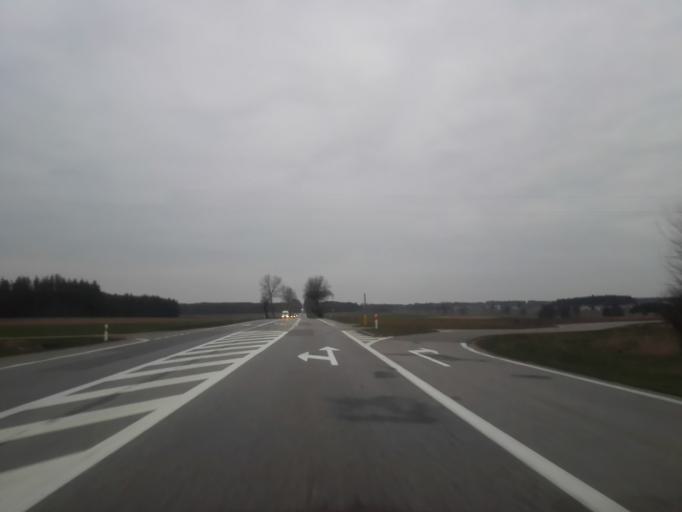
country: PL
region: Podlasie
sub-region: Powiat kolnenski
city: Stawiski
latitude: 53.3230
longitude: 22.1528
